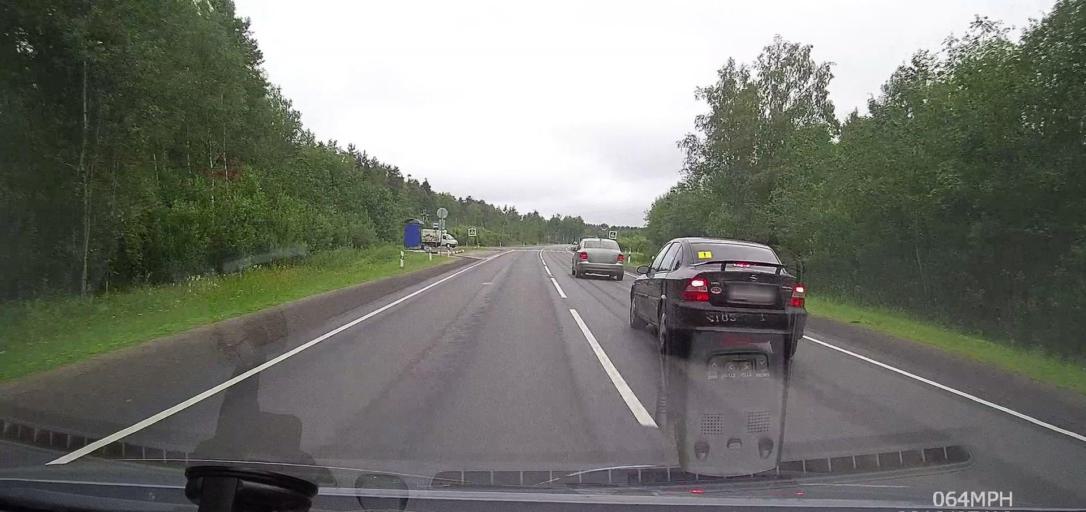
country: RU
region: Leningrad
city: Syas'stroy
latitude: 60.2035
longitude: 32.6754
